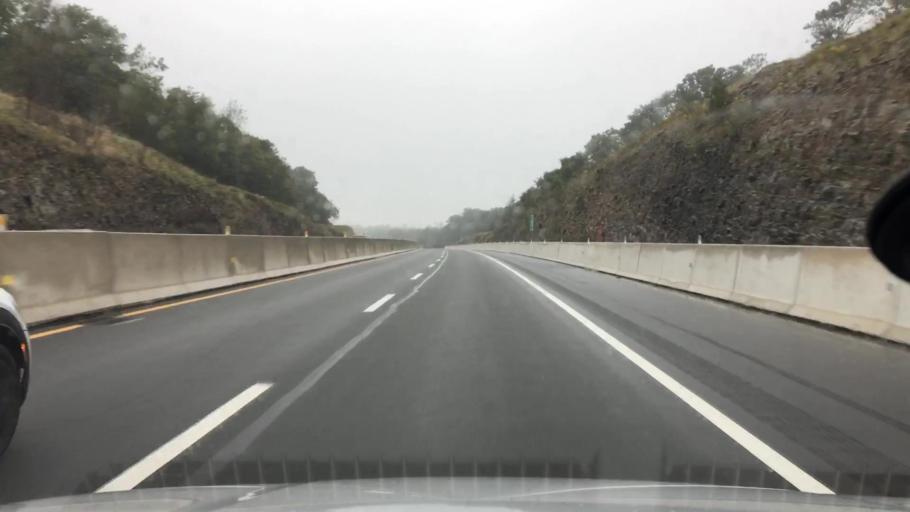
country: US
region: Pennsylvania
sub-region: Luzerne County
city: Mountain Top
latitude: 41.1687
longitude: -75.7766
